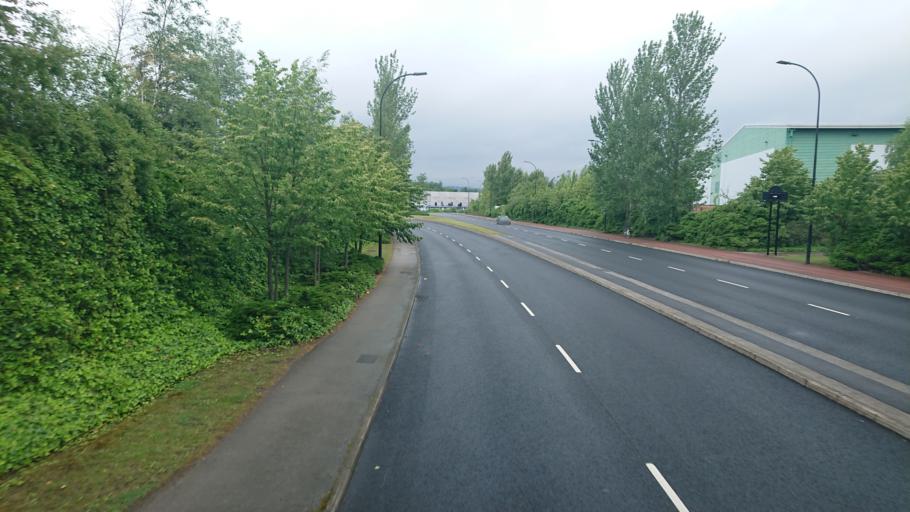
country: GB
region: England
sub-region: Rotherham
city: Orgreave
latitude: 53.3999
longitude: -1.4068
